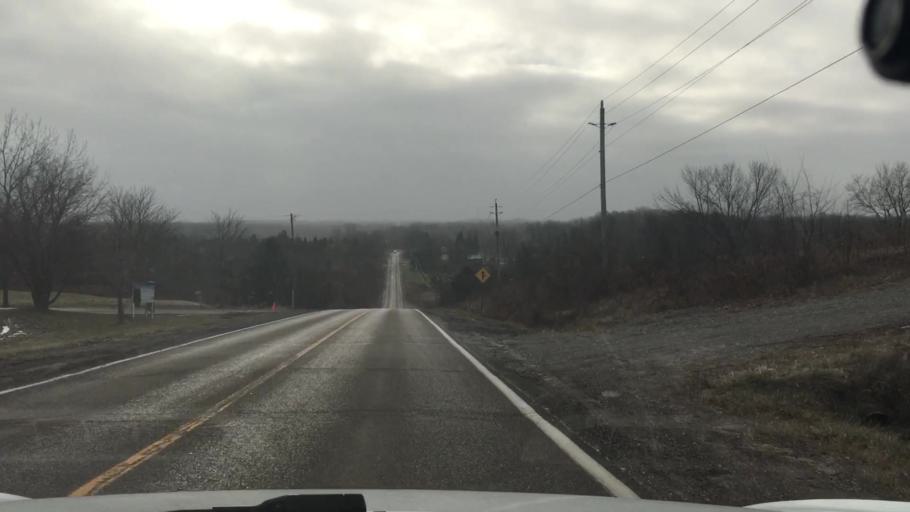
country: CA
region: Ontario
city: Oshawa
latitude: 43.9380
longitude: -78.8004
